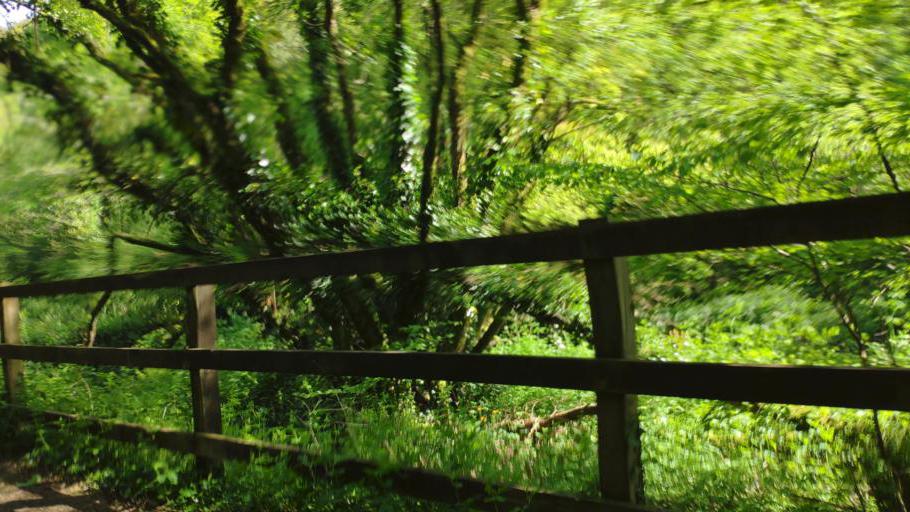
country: IE
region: Munster
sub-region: County Cork
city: Blarney
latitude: 51.9415
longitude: -8.5643
